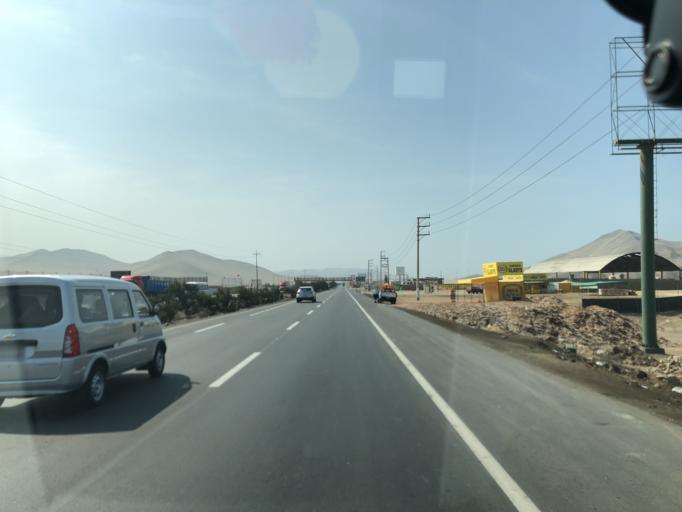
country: PE
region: Lima
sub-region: Provincia de Canete
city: Chilca
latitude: -12.5369
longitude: -76.7195
